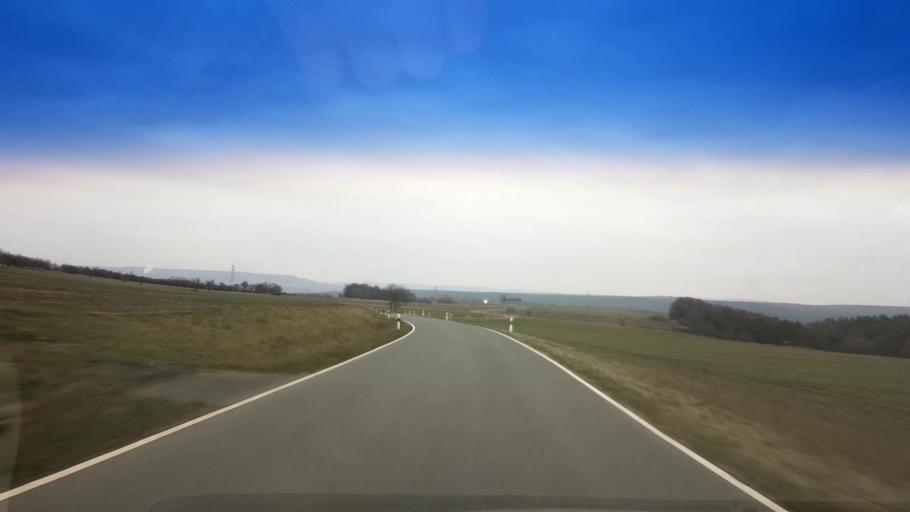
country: DE
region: Bavaria
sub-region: Upper Franconia
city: Hallerndorf
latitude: 49.7673
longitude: 10.9536
